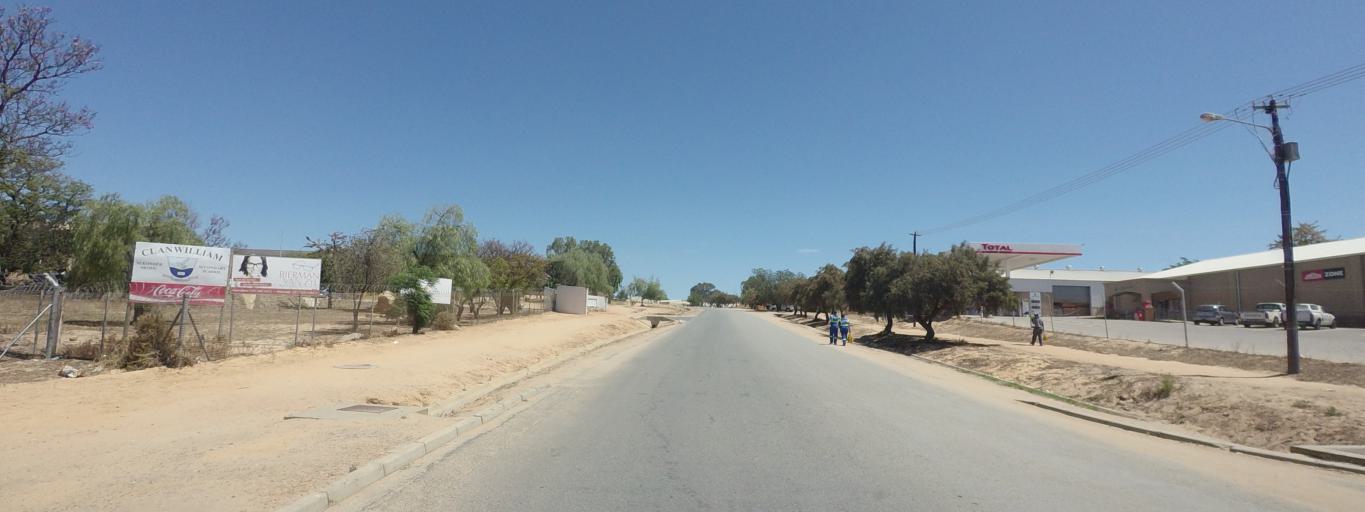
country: ZA
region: Western Cape
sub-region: West Coast District Municipality
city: Clanwilliam
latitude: -32.1882
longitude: 18.8897
